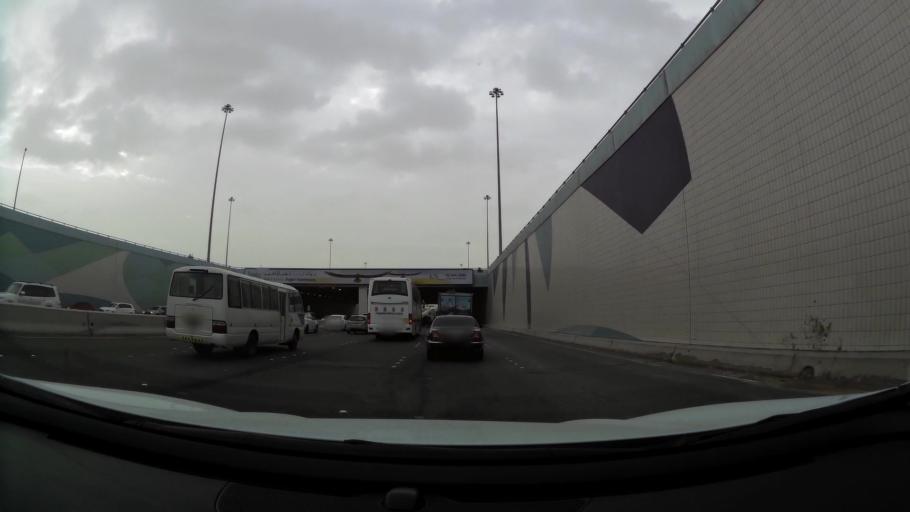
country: AE
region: Abu Dhabi
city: Abu Dhabi
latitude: 24.4732
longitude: 54.3914
